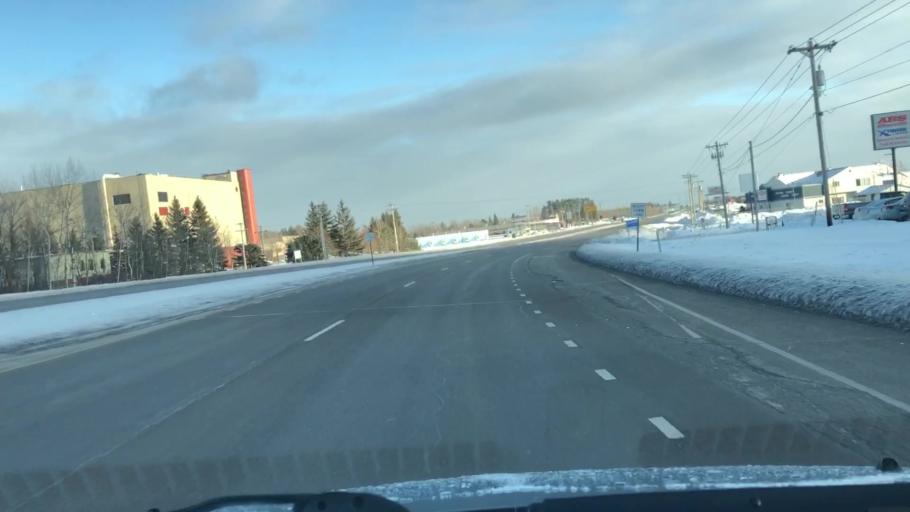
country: US
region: Minnesota
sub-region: Saint Louis County
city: Hermantown
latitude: 46.8362
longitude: -92.2103
